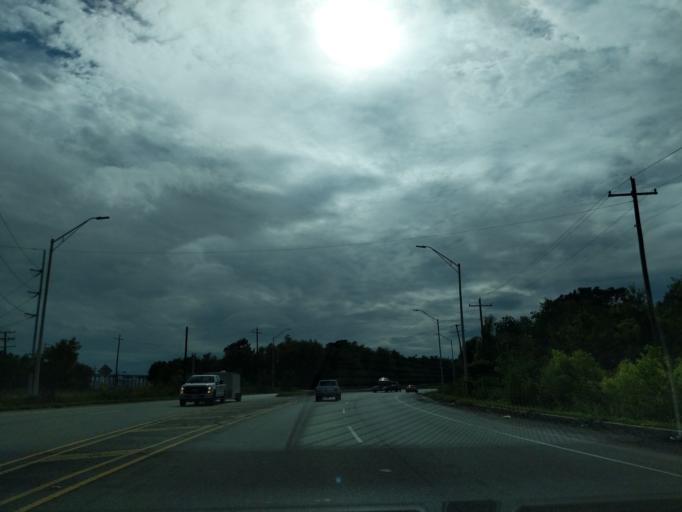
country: US
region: Louisiana
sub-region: Saint Bernard Parish
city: Chalmette
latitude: 30.0177
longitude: -89.9316
